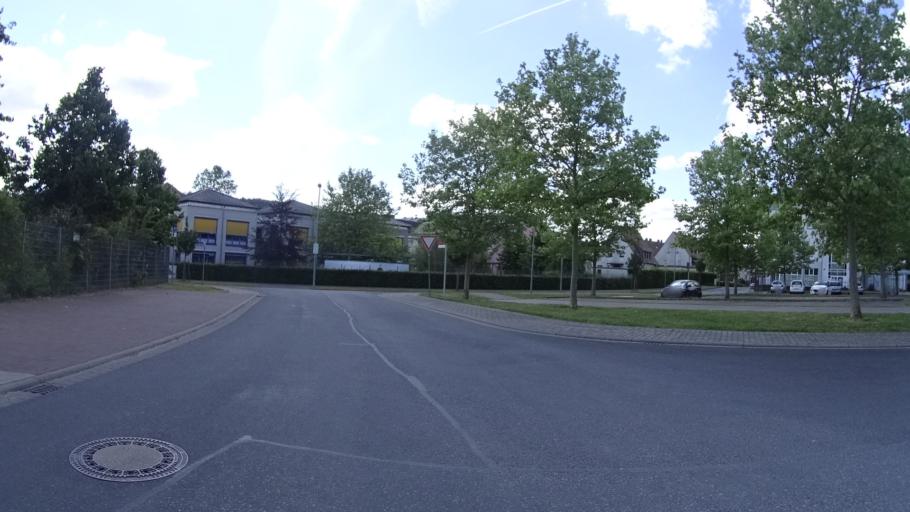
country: DE
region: Bavaria
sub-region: Regierungsbezirk Unterfranken
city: Worth am Main
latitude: 49.8049
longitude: 9.1551
